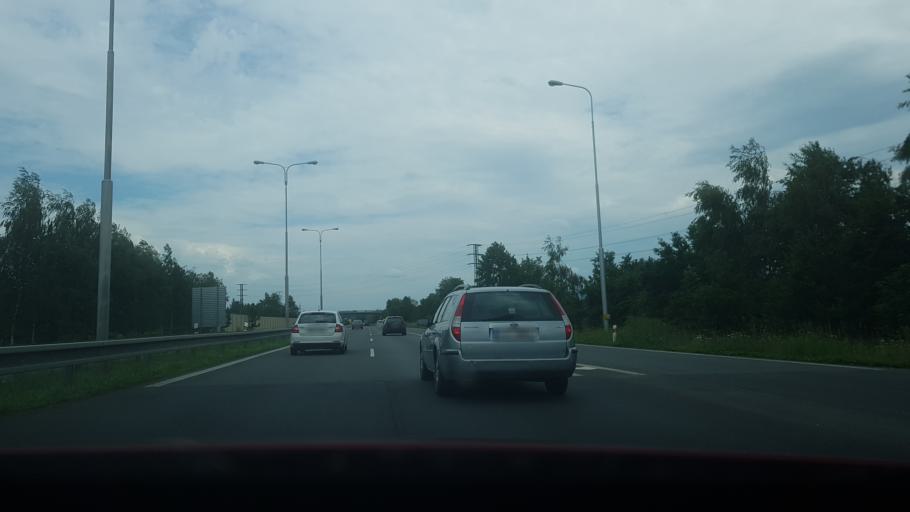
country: CZ
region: Moravskoslezsky
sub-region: Okres Frydek-Mistek
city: Stare Mesto
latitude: 49.6830
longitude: 18.3712
